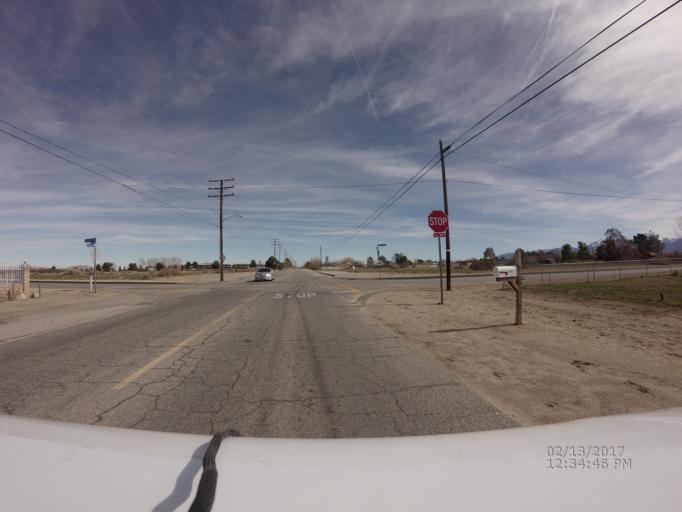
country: US
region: California
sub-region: Los Angeles County
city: Littlerock
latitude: 34.5726
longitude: -117.9434
